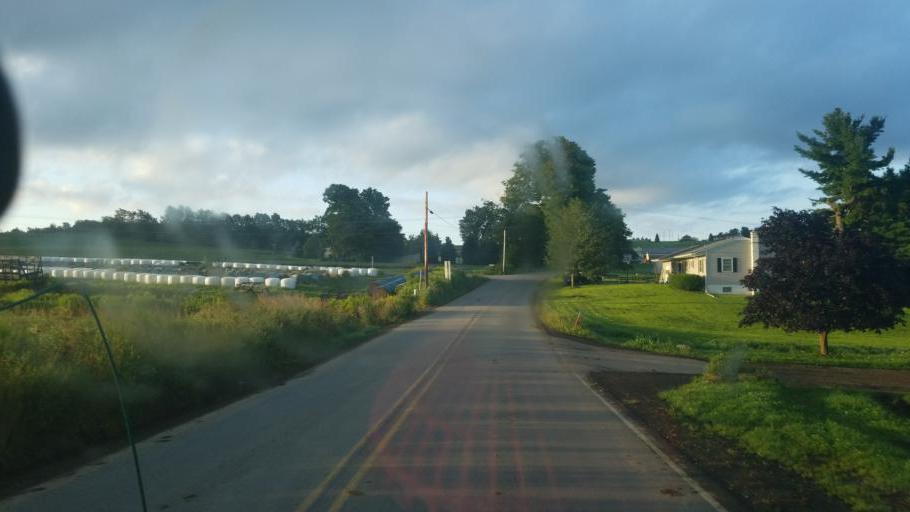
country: US
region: Pennsylvania
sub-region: Potter County
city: Galeton
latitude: 41.8877
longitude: -77.7614
